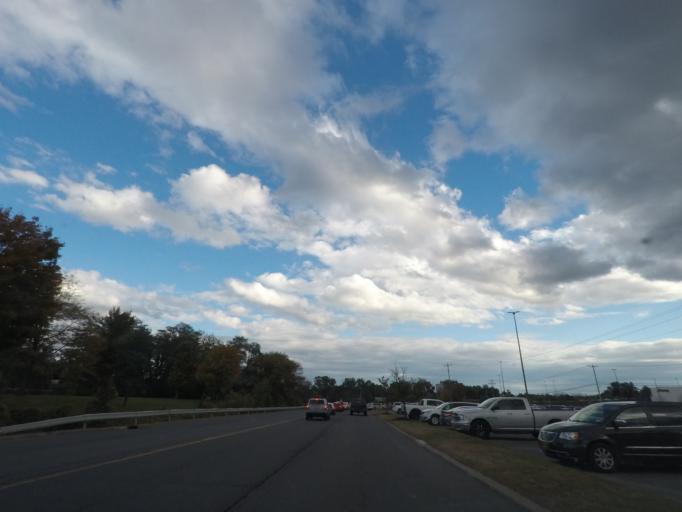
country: US
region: New York
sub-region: Albany County
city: McKownville
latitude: 42.6908
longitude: -73.8475
